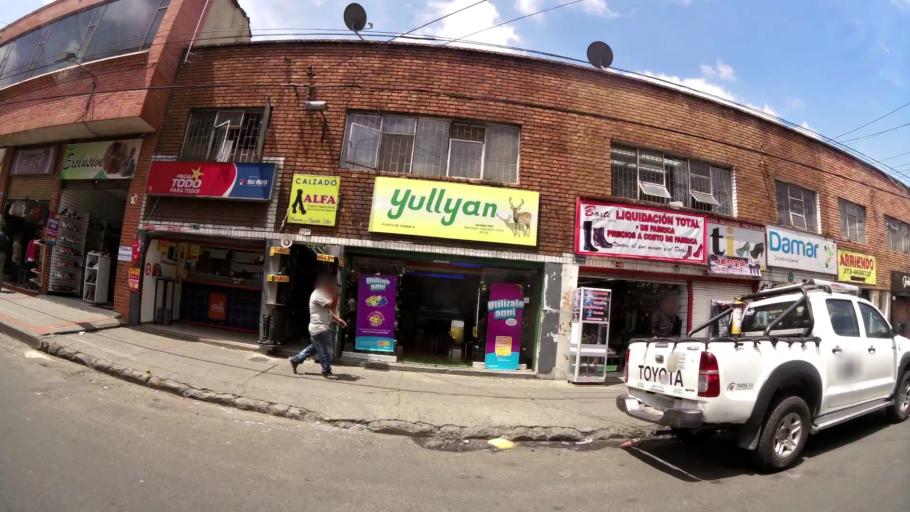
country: CO
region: Bogota D.C.
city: Bogota
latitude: 4.6058
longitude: -74.0909
